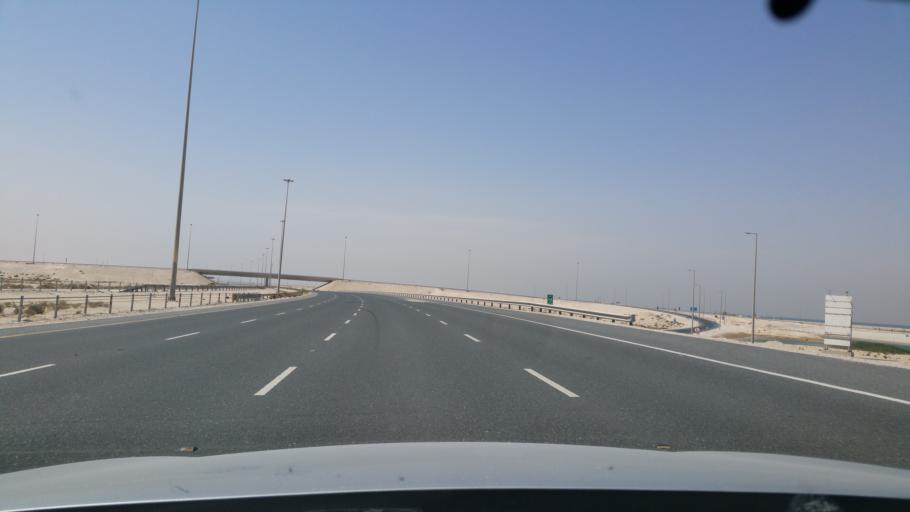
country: QA
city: Umm Bab
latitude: 24.8420
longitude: 50.8738
